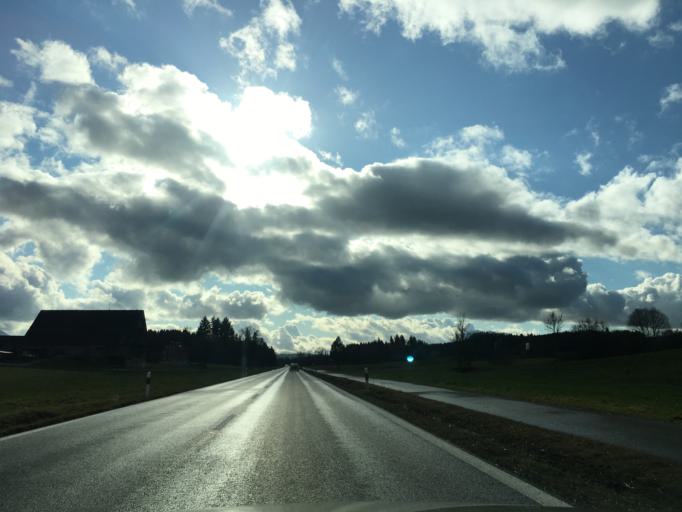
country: CH
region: Aargau
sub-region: Bezirk Muri
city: Sins
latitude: 47.1803
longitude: 8.3957
